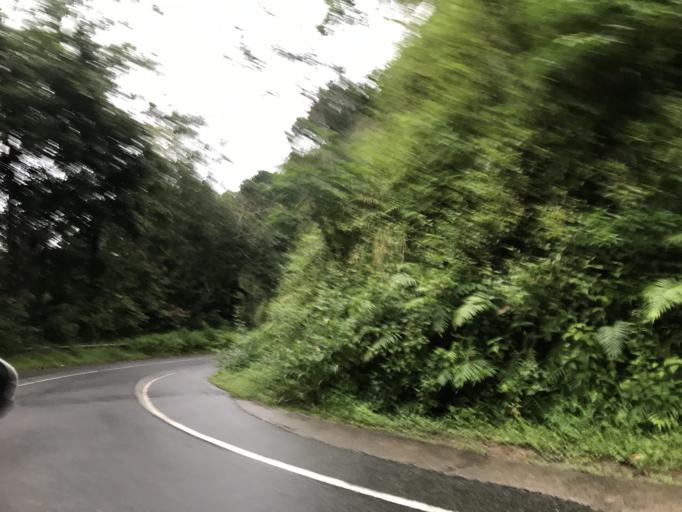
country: LK
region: Sabaragamuwa
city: Ratnapura
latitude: 6.5393
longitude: 80.3012
